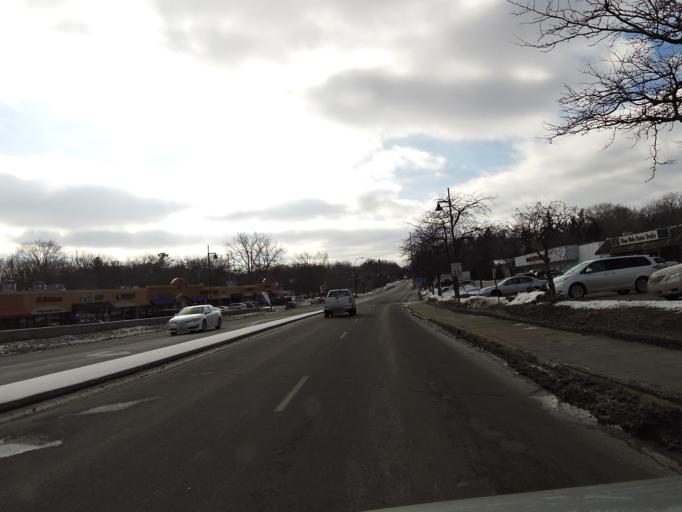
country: US
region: Minnesota
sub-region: Hennepin County
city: Hopkins
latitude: 44.9043
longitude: -93.4659
